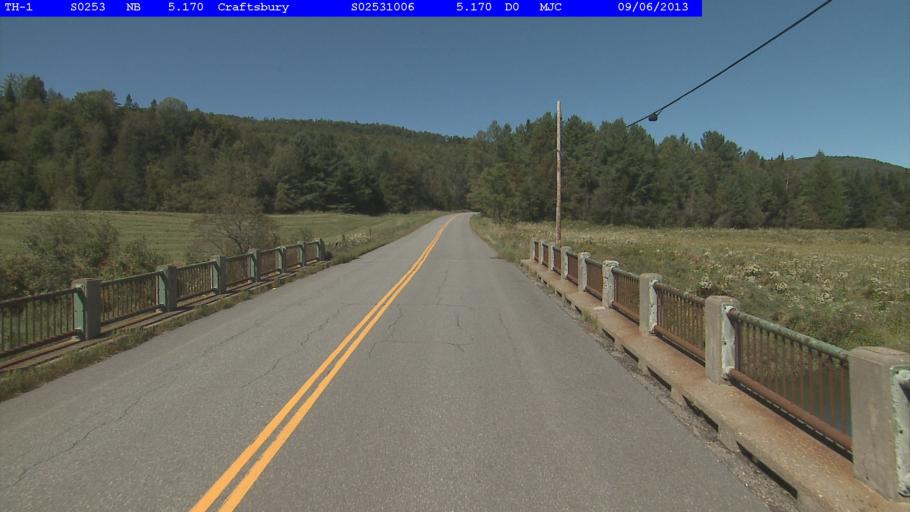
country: US
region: Vermont
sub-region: Caledonia County
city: Hardwick
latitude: 44.6770
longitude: -72.4005
